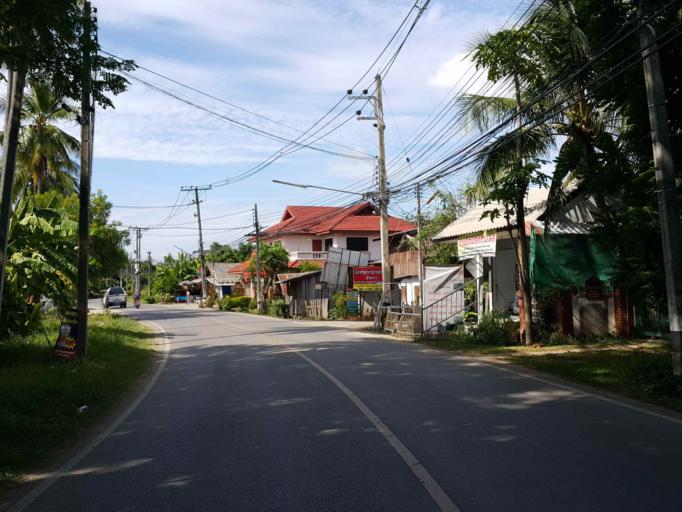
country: TH
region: Chiang Mai
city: Saraphi
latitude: 18.7369
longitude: 98.9896
